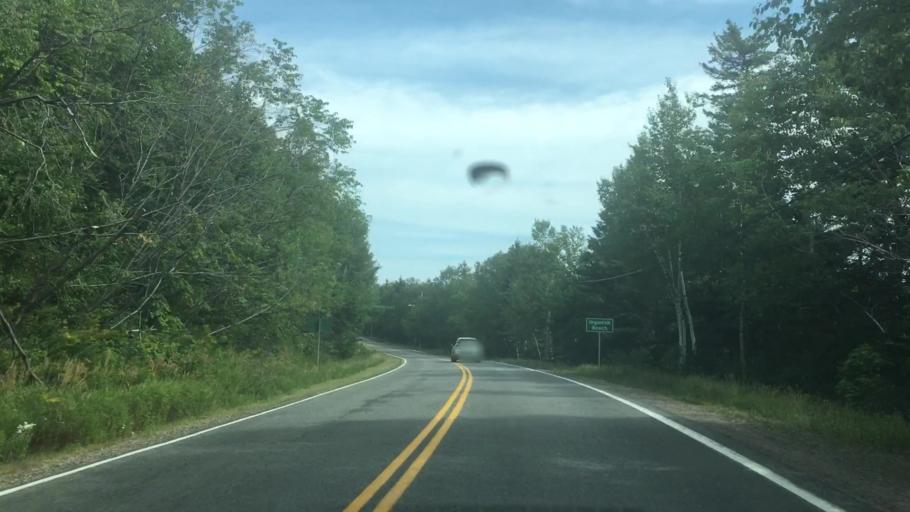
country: CA
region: Nova Scotia
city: Sydney Mines
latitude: 46.6356
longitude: -60.4188
